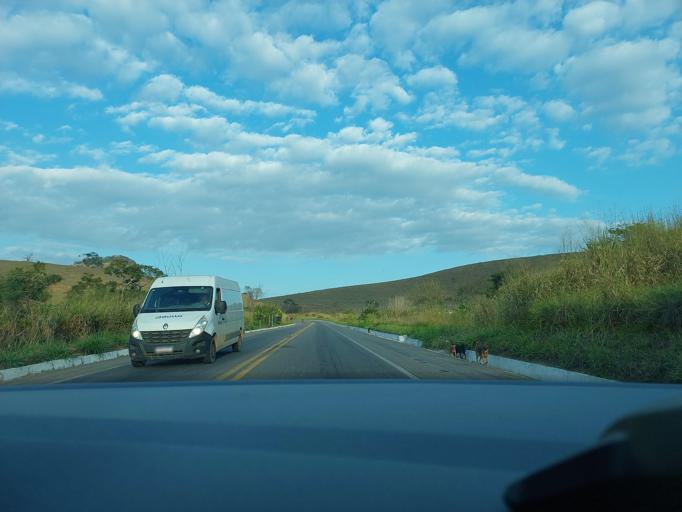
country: BR
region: Minas Gerais
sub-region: Muriae
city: Muriae
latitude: -21.1266
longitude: -42.3274
